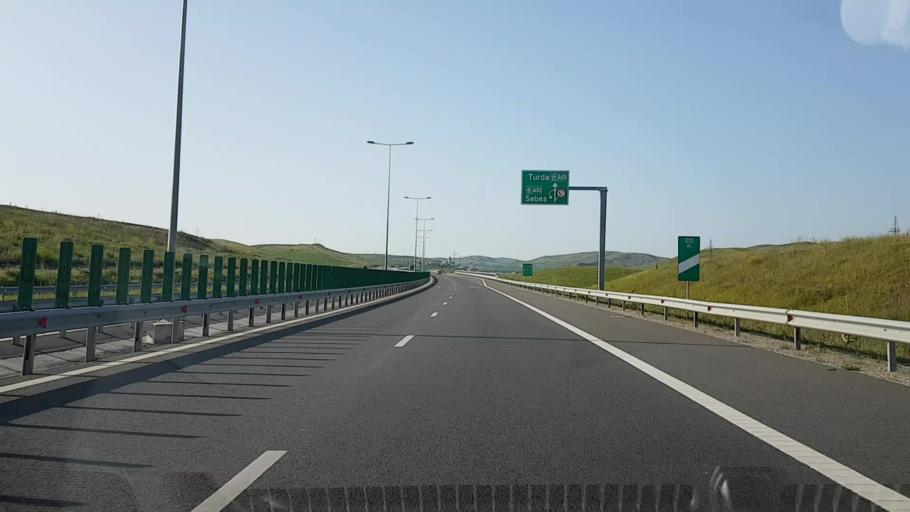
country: RO
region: Alba
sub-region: Comuna Unirea
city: Unirea
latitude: 46.4160
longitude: 23.7997
